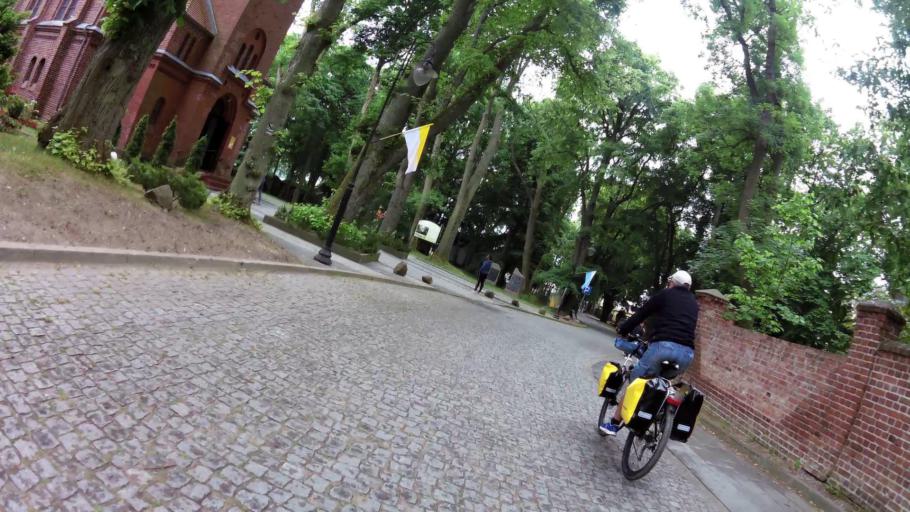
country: PL
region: West Pomeranian Voivodeship
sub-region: Powiat gryficki
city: Rewal
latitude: 54.0750
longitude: 14.9934
